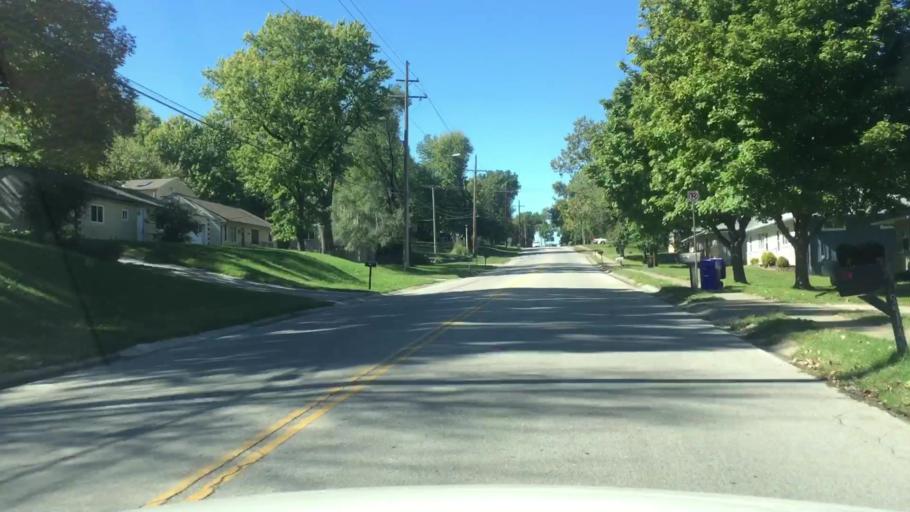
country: US
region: Kansas
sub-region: Johnson County
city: Merriam
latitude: 39.0296
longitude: -94.6967
